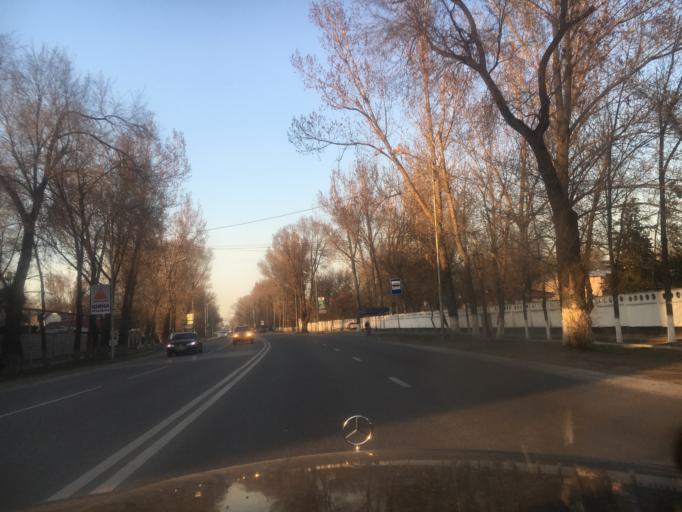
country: KZ
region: Almaty Oblysy
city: Pervomayskiy
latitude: 43.3663
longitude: 76.9861
